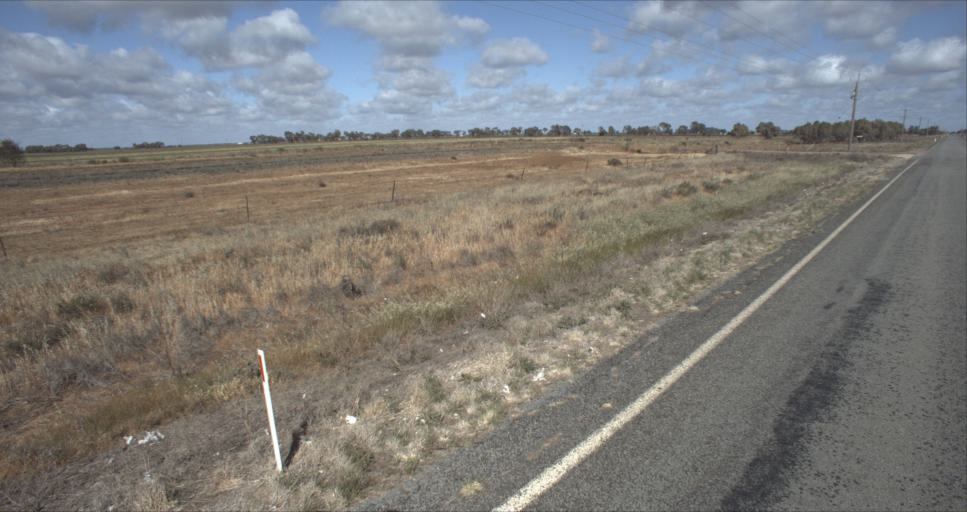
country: AU
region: New South Wales
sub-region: Leeton
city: Leeton
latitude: -34.5411
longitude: 146.2465
